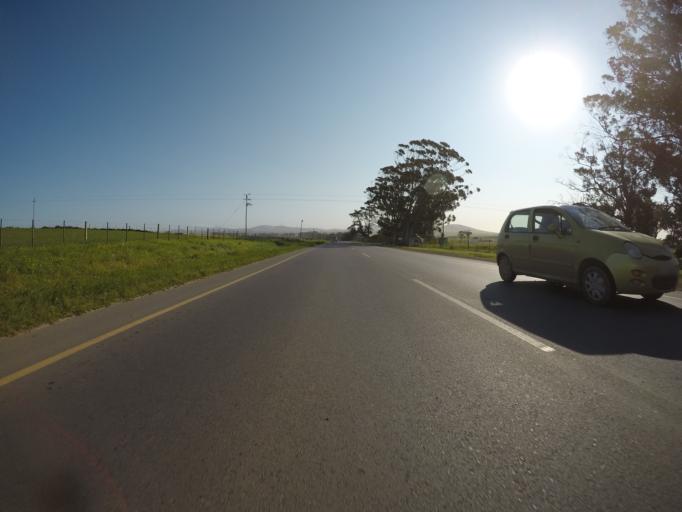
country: ZA
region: Western Cape
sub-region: City of Cape Town
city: Kraaifontein
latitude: -33.7770
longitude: 18.7331
